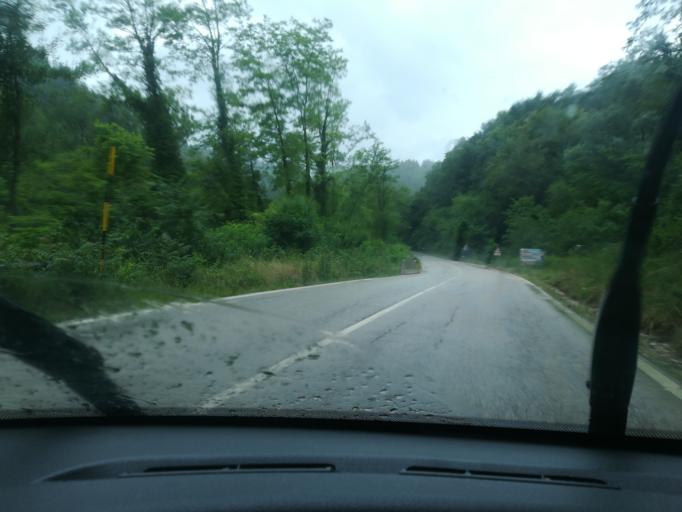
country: IT
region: The Marches
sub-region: Province of Fermo
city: Amandola
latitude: 42.9843
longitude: 13.3452
